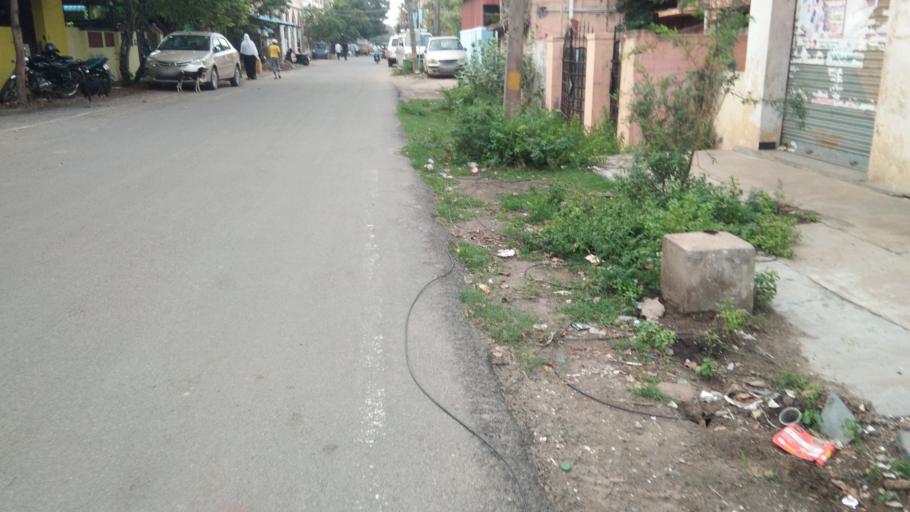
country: IN
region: Tamil Nadu
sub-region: Kancheepuram
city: Pallavaram
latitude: 12.9644
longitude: 80.1421
